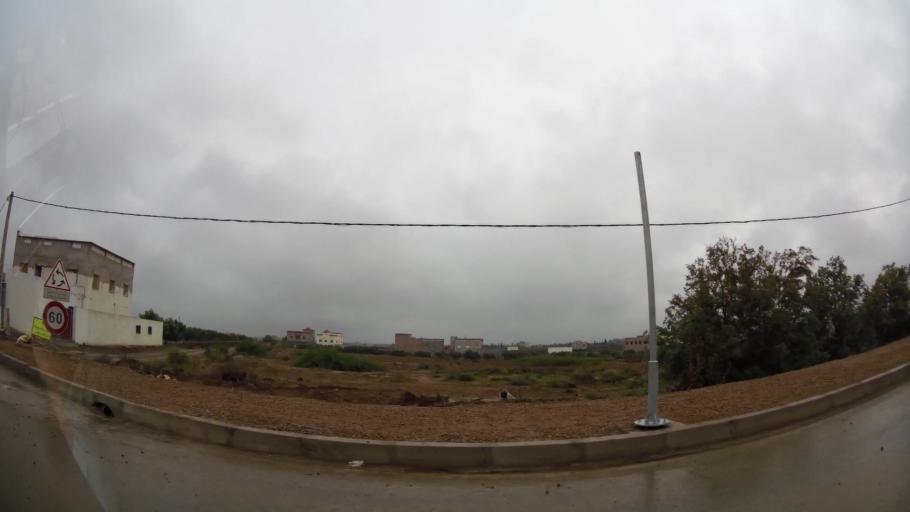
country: MA
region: Taza-Al Hoceima-Taounate
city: Imzourene
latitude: 35.1602
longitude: -3.8542
